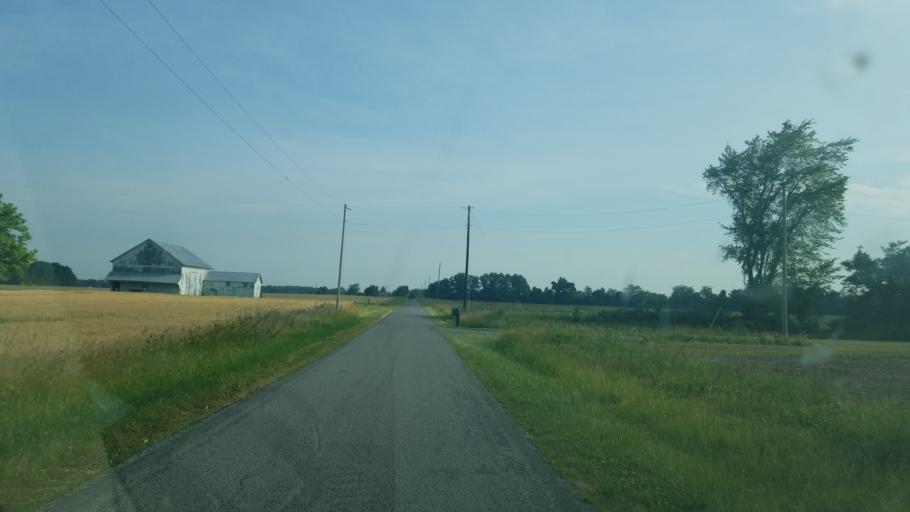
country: US
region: Ohio
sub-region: Hancock County
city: Arlington
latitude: 40.8444
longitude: -83.6703
